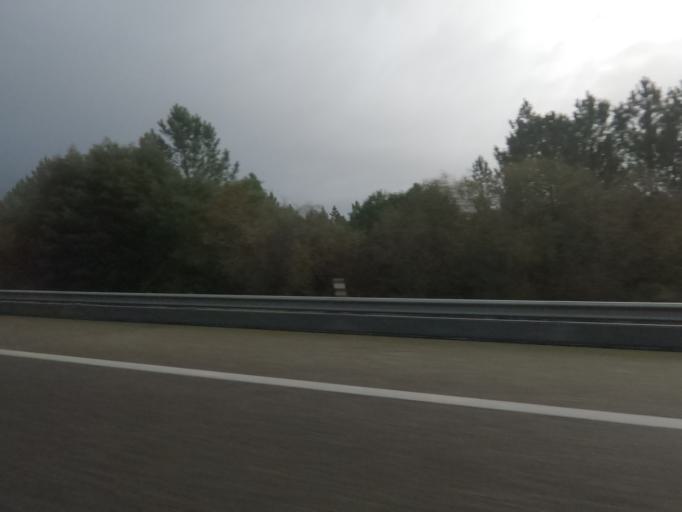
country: PT
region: Viana do Castelo
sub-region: Ponte de Lima
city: Ponte de Lima
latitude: 41.8181
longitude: -8.5998
